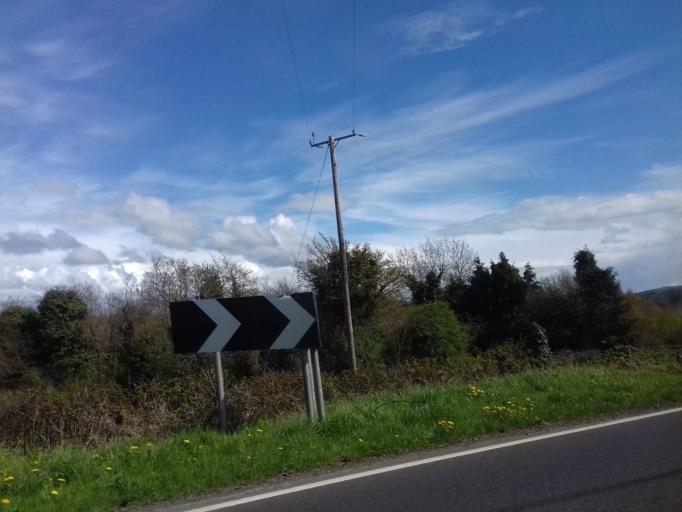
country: GB
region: Northern Ireland
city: Irvinestown
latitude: 54.4446
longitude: -7.7930
